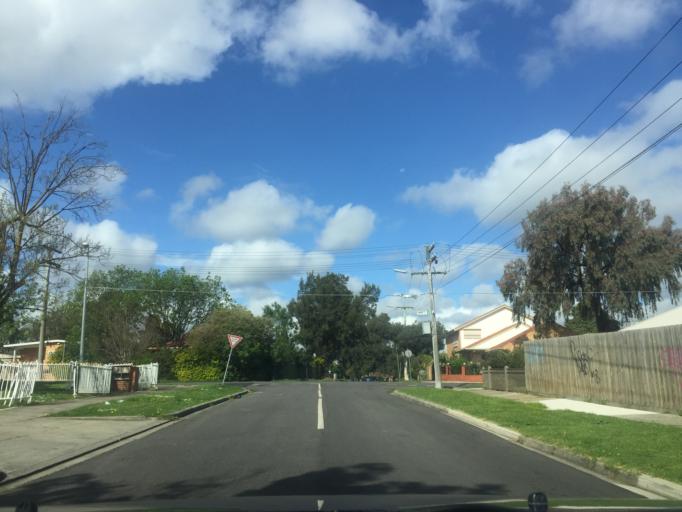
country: AU
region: Victoria
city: Heidelberg West
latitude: -37.7387
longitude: 145.0381
